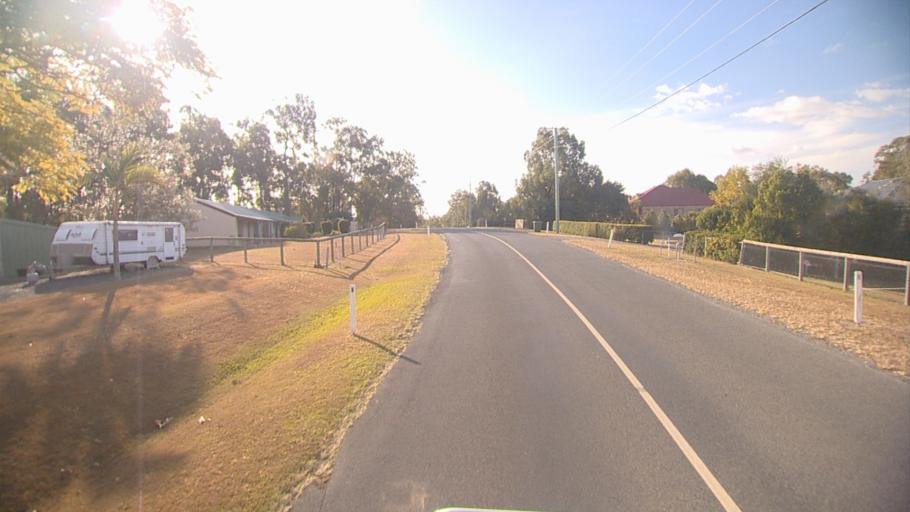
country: AU
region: Queensland
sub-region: Logan
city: Cedar Vale
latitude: -27.8741
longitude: 153.0109
